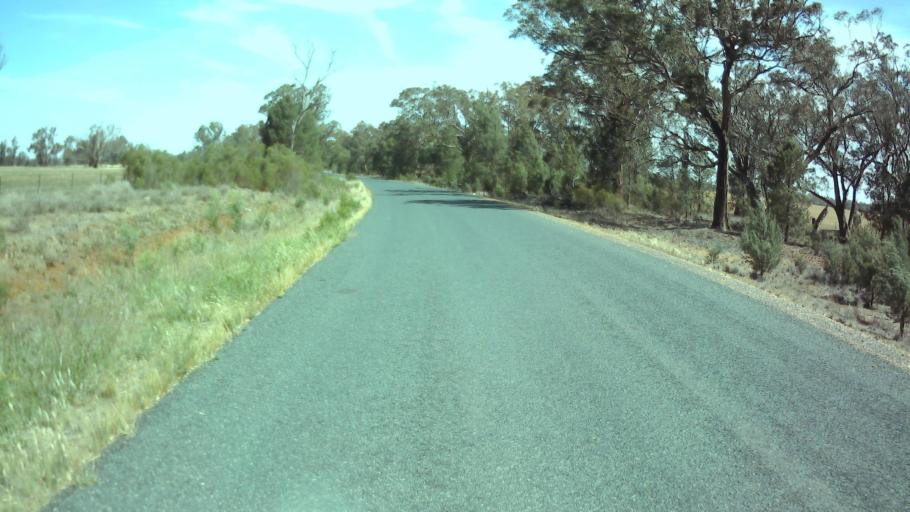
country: AU
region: New South Wales
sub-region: Weddin
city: Grenfell
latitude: -34.0551
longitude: 148.1299
